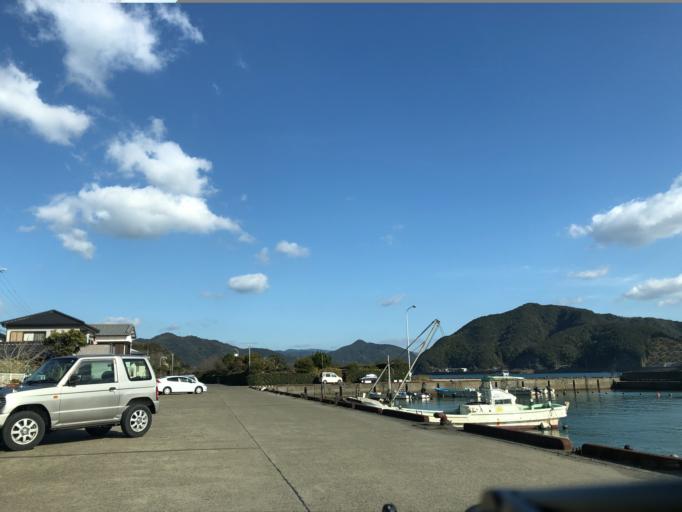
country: JP
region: Kochi
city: Sukumo
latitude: 32.9146
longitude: 132.7042
